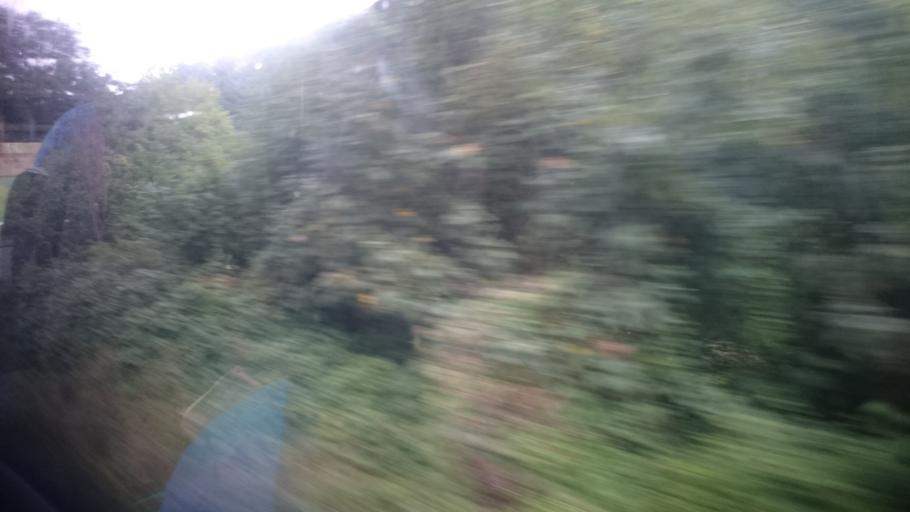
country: ES
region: Asturias
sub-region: Province of Asturias
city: Amieva
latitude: 43.3145
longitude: -5.0676
